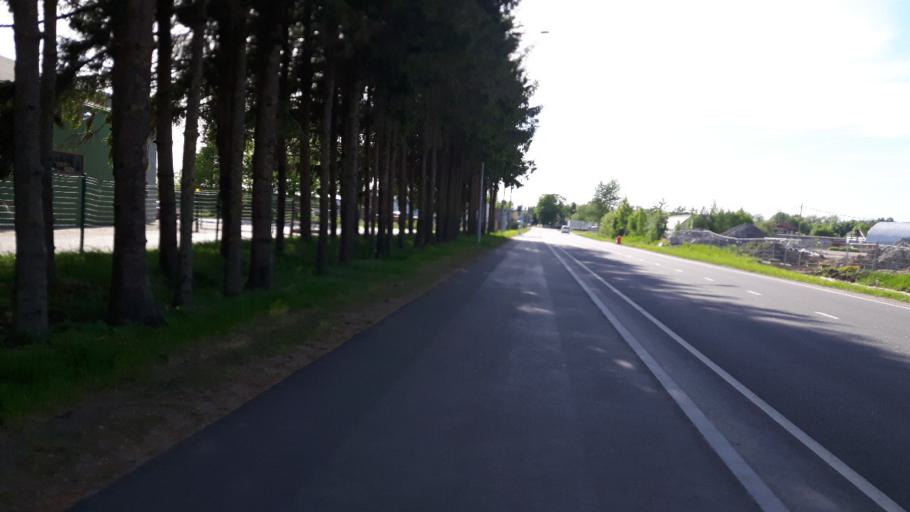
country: EE
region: Harju
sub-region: Joelaehtme vald
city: Loo
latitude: 59.4310
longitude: 24.9603
